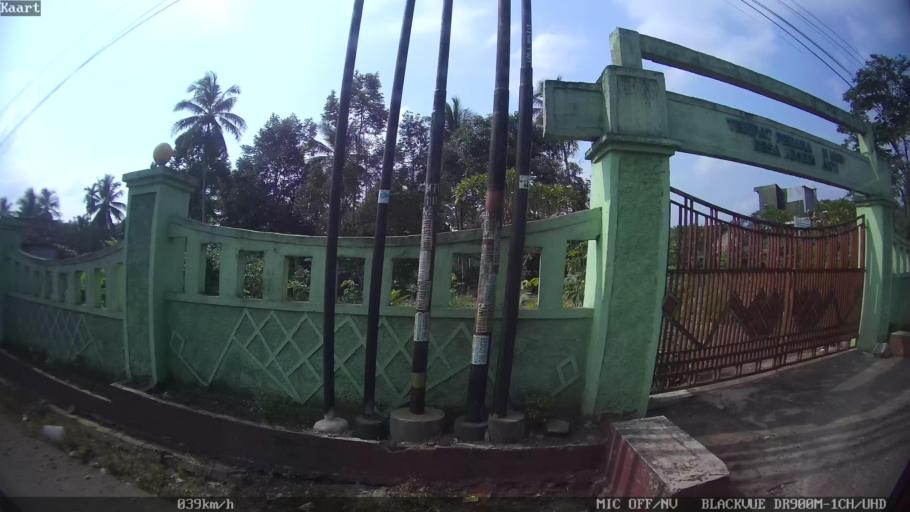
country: ID
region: Lampung
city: Natar
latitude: -5.3646
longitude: 105.1837
